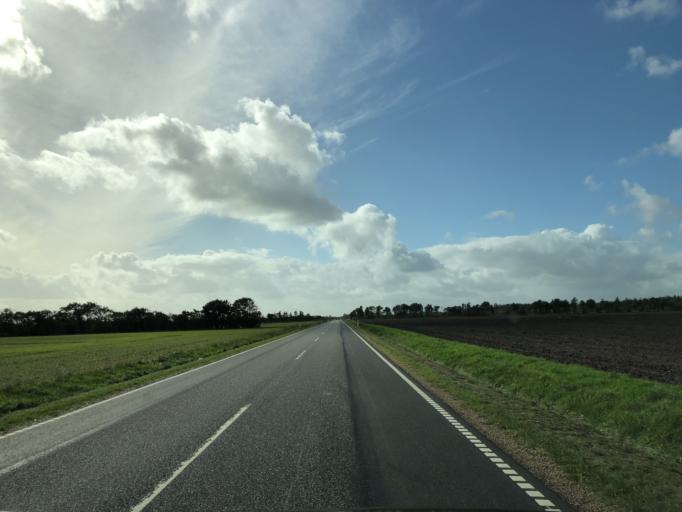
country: DK
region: Central Jutland
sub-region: Holstebro Kommune
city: Holstebro
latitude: 56.3692
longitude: 8.4734
